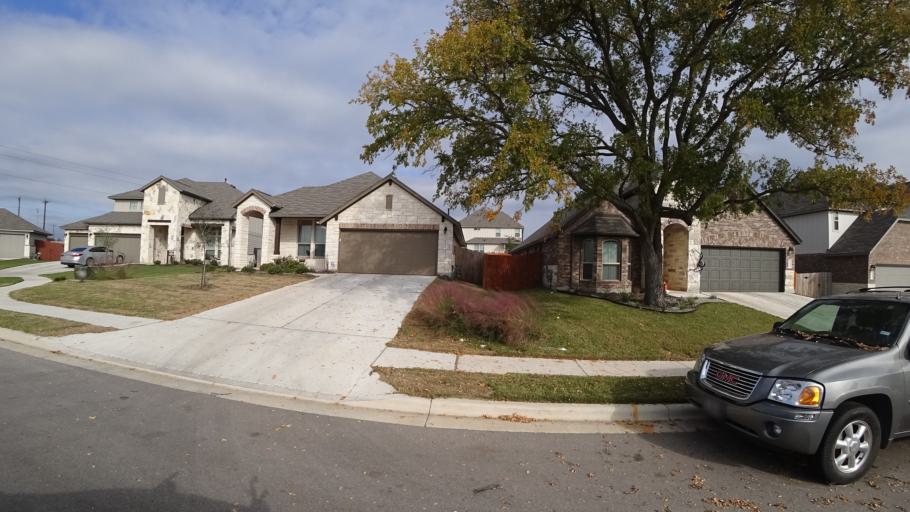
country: US
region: Texas
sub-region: Travis County
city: Manchaca
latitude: 30.1321
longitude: -97.8489
